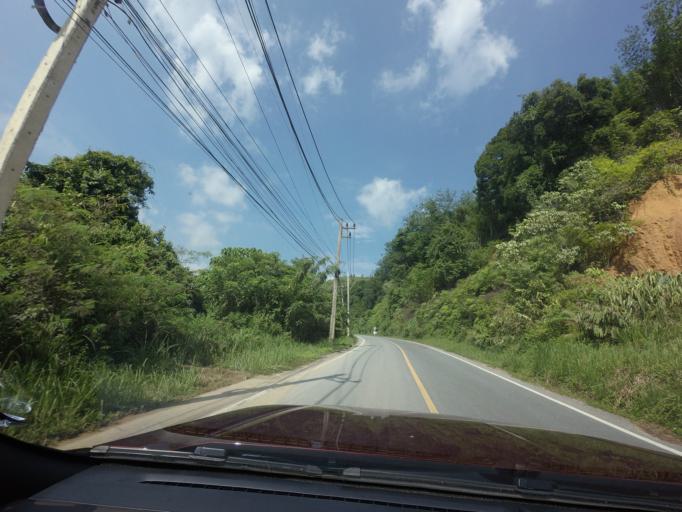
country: TH
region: Yala
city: Betong
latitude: 5.9250
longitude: 101.1810
